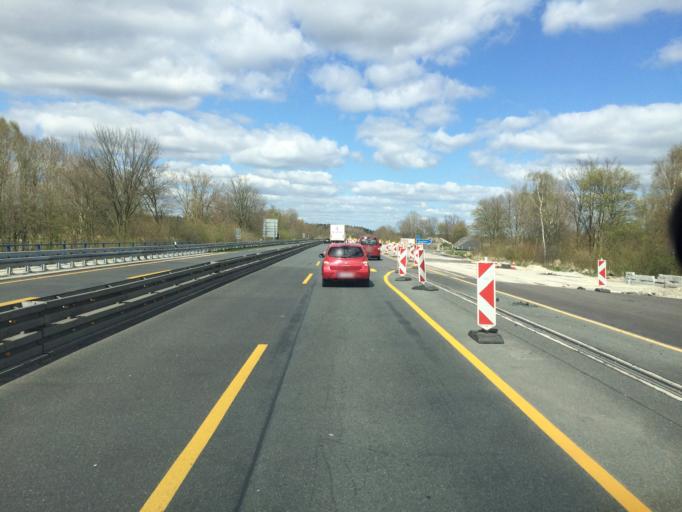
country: DE
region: North Rhine-Westphalia
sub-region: Regierungsbezirk Munster
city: Legden
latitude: 52.0530
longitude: 7.0628
